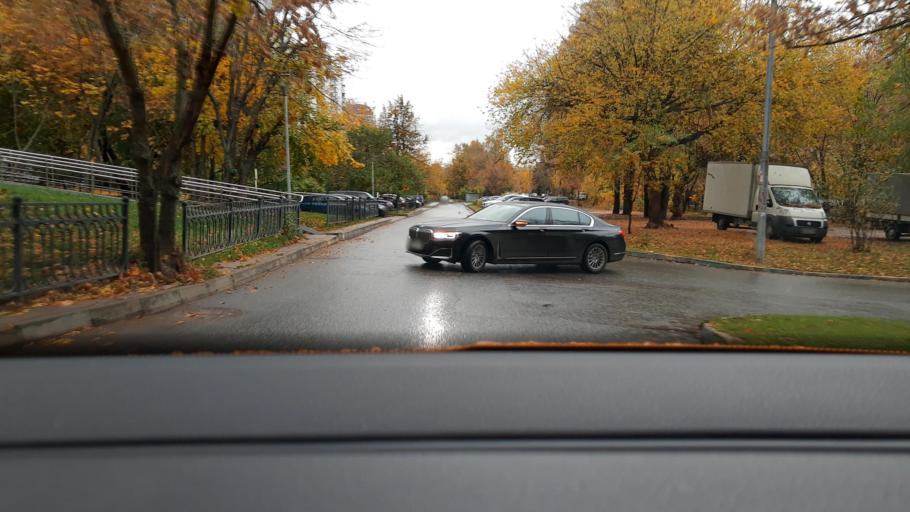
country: RU
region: Moscow
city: Strogino
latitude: 55.8137
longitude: 37.4000
